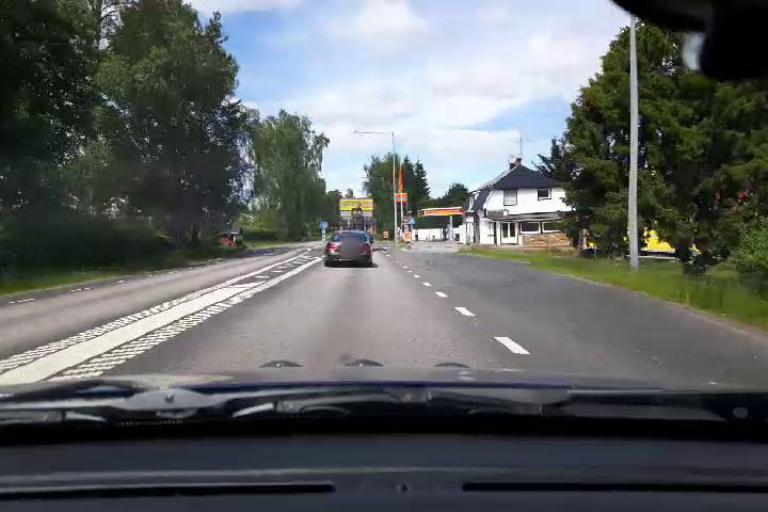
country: SE
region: Uppsala
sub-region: Osthammars Kommun
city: Bjorklinge
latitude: 60.0359
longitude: 17.5514
